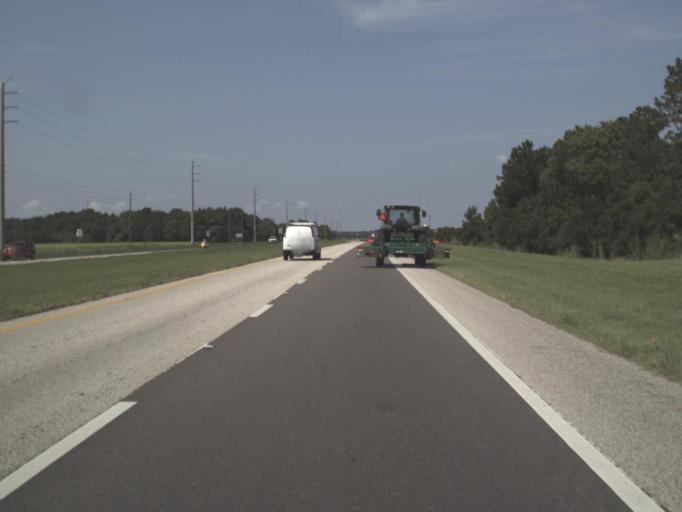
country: US
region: Florida
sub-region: Putnam County
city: East Palatka
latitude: 29.6785
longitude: -81.5804
